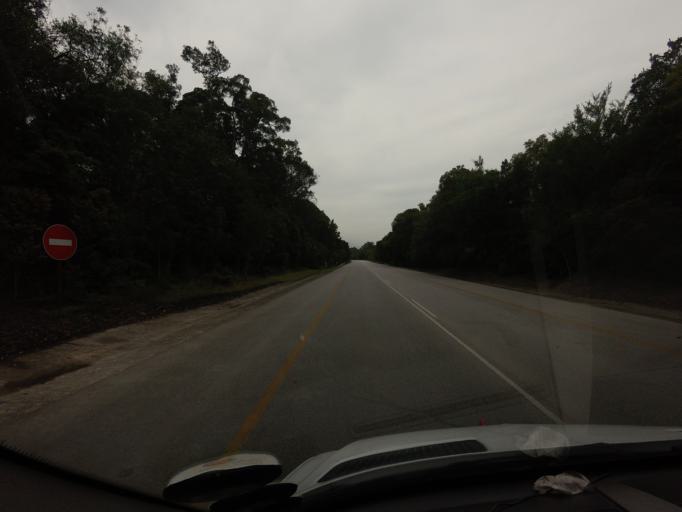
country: ZA
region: Eastern Cape
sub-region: Cacadu District Municipality
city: Kareedouw
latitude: -33.9696
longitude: 23.8538
